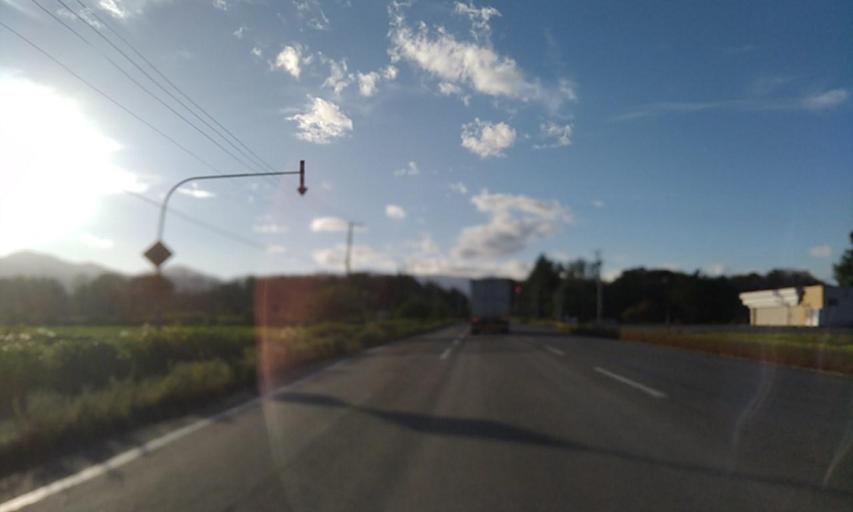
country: JP
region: Hokkaido
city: Otofuke
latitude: 42.9588
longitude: 142.9094
